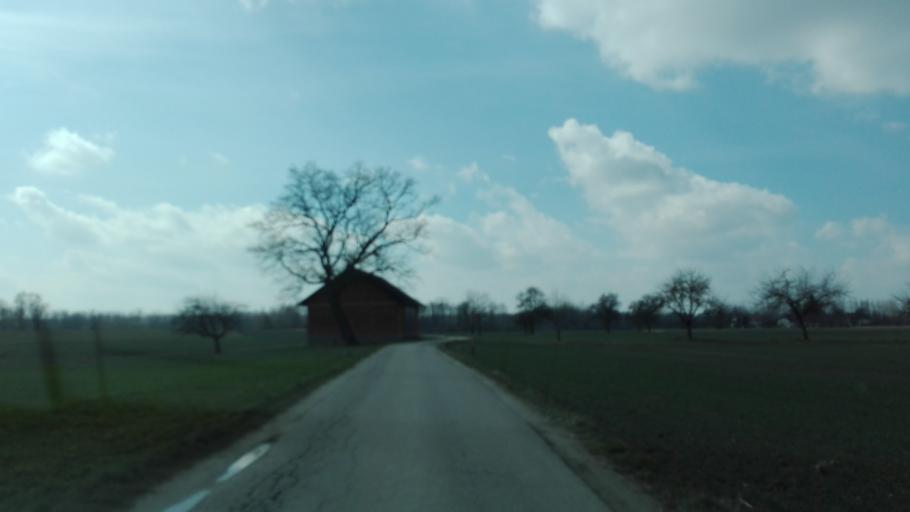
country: AT
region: Upper Austria
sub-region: Politischer Bezirk Urfahr-Umgebung
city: Ottensheim
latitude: 48.3262
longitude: 14.1488
